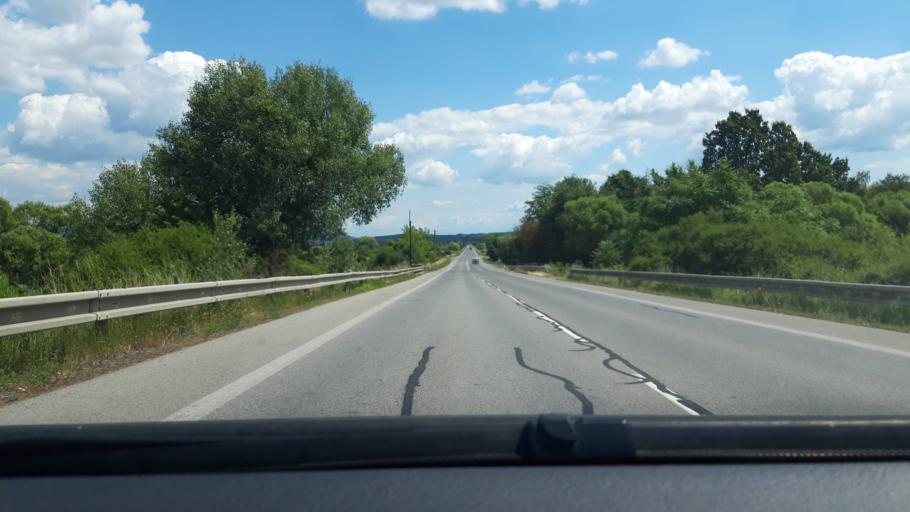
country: SK
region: Banskobystricky
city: Lucenec
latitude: 48.3067
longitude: 19.7195
